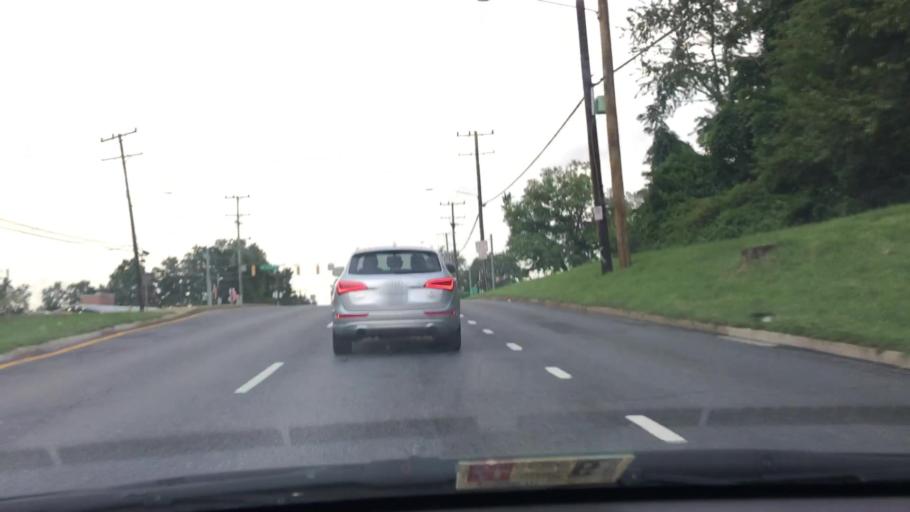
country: US
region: Maryland
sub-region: Montgomery County
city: Aspen Hill
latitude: 39.0610
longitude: -77.0908
